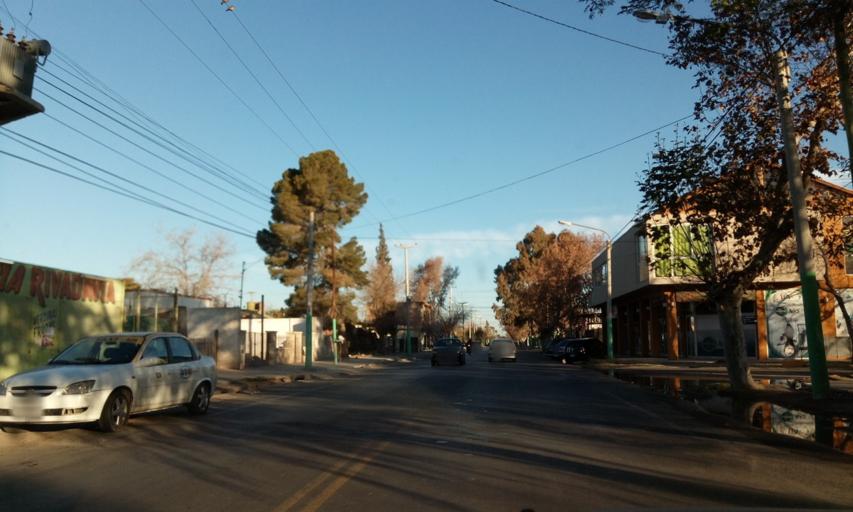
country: AR
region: San Juan
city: San Juan
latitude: -31.5339
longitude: -68.5936
